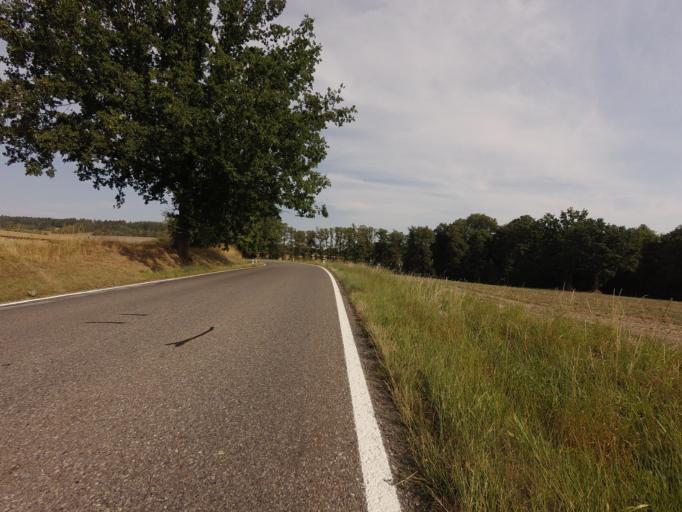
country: CZ
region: Jihocesky
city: Milevsko
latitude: 49.4921
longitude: 14.3639
